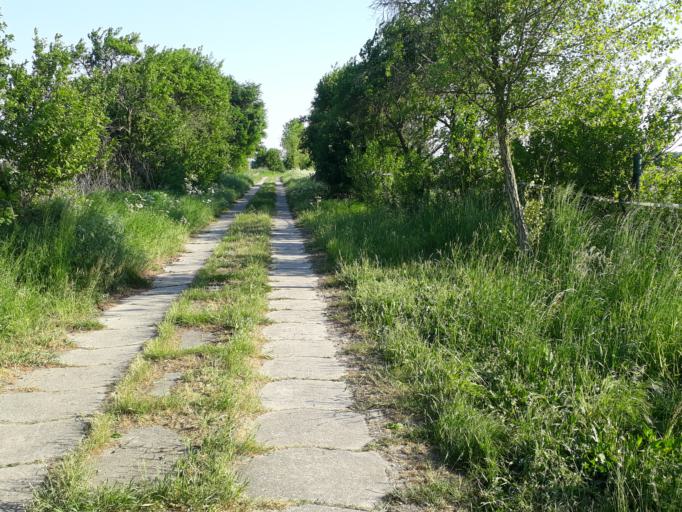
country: DE
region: Brandenburg
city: Potsdam
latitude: 52.4602
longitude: 13.0070
